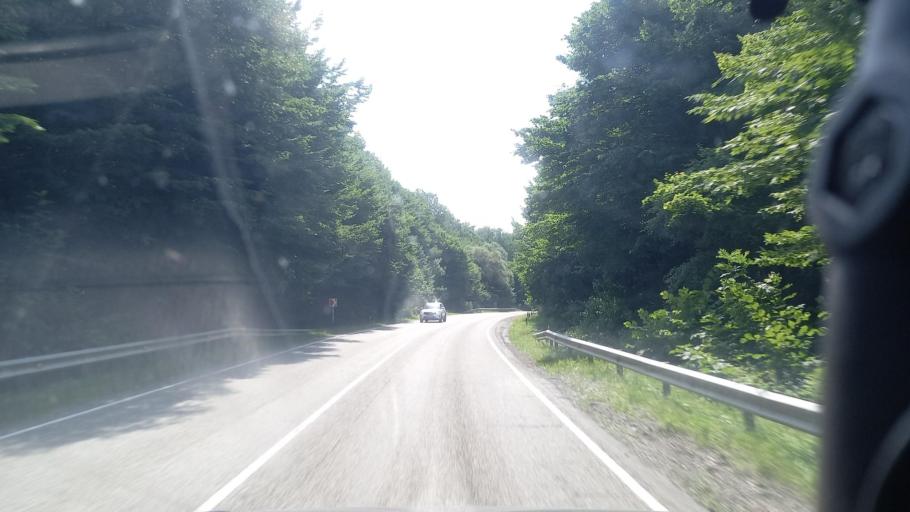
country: RU
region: Krasnodarskiy
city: Psebay
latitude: 44.0751
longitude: 40.8534
